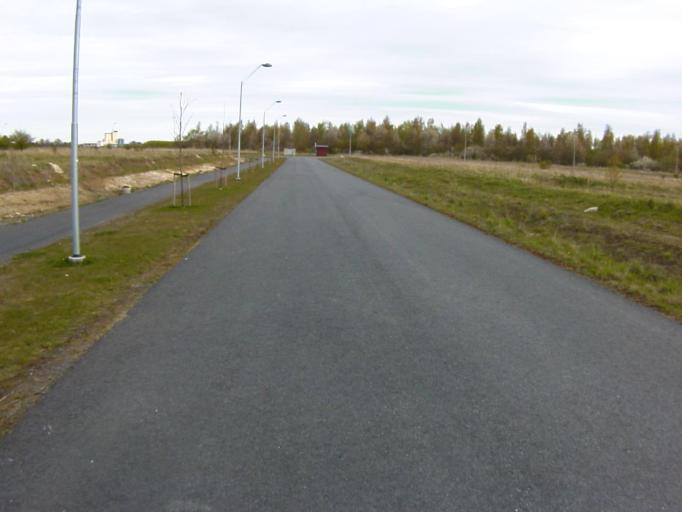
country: SE
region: Skane
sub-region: Kristianstads Kommun
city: Kristianstad
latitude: 56.0245
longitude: 14.1160
